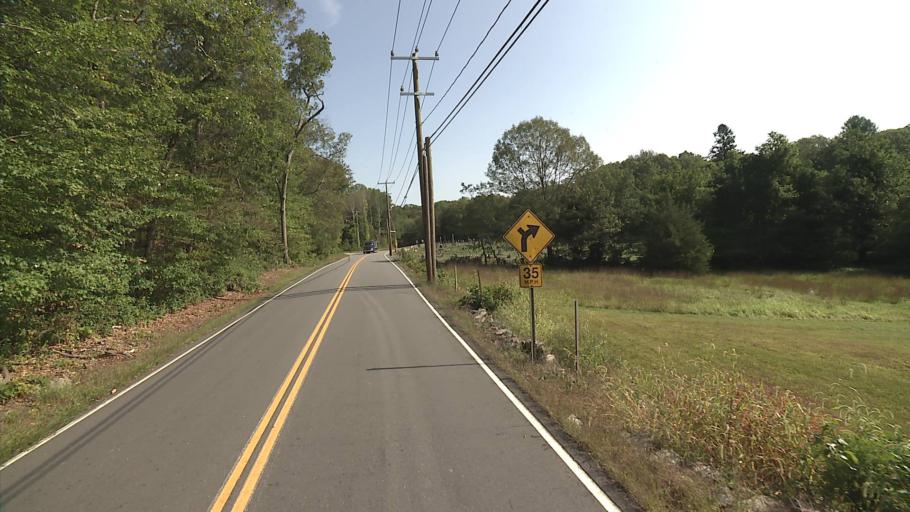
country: US
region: Connecticut
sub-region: New London County
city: Lisbon
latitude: 41.5788
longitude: -72.0283
